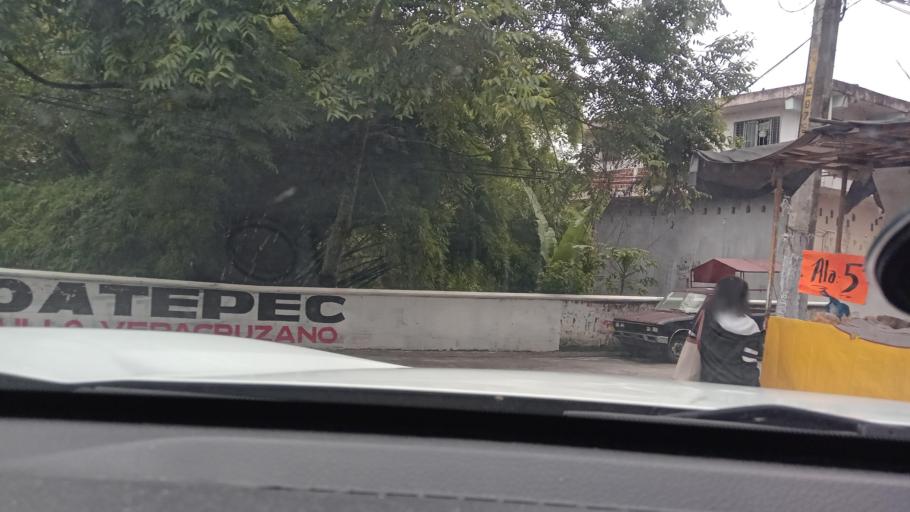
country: MX
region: Veracruz
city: Coatepec
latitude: 19.4484
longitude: -96.9617
